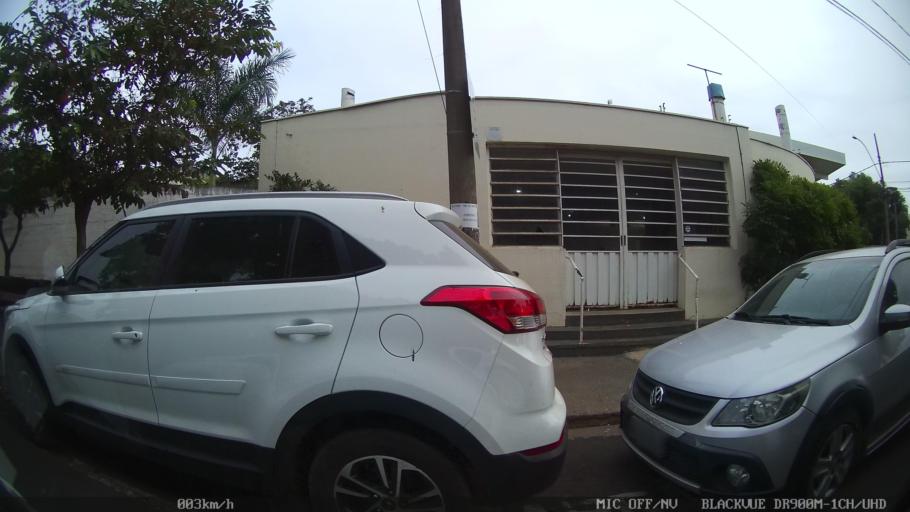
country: BR
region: Sao Paulo
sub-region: Sao Jose Do Rio Preto
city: Sao Jose do Rio Preto
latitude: -20.8303
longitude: -49.3956
